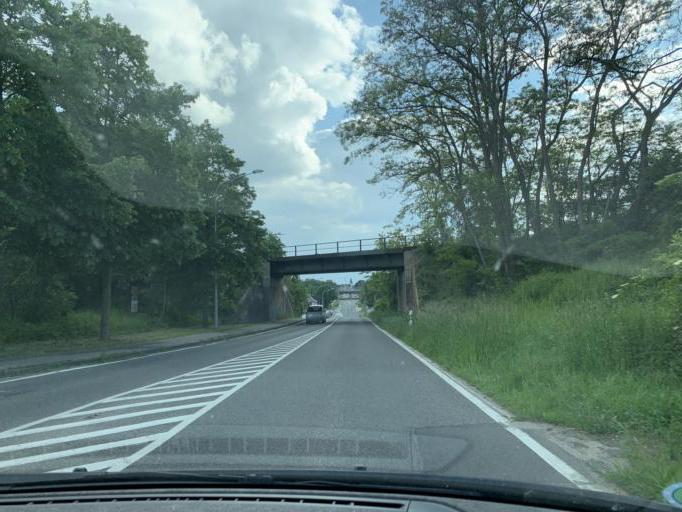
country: DE
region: North Rhine-Westphalia
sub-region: Regierungsbezirk Koln
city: Weilerswist
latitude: 50.7670
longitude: 6.8499
